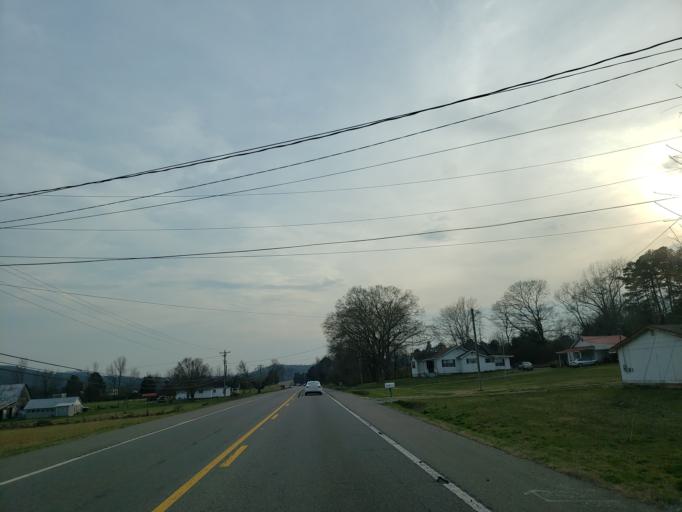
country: US
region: Tennessee
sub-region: Bradley County
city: Wildwood Lake
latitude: 35.0907
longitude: -84.8825
